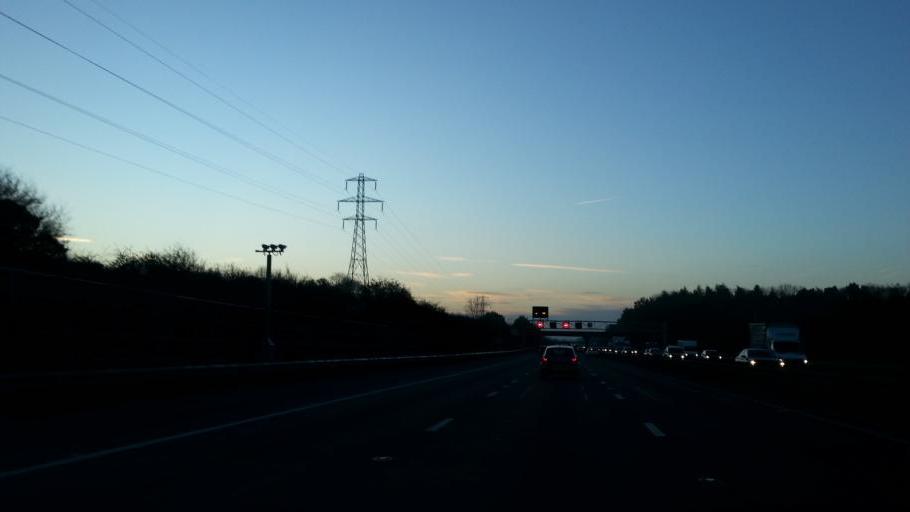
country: GB
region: England
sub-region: Central Bedfordshire
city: Steppingley
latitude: 52.0021
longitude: -0.5440
